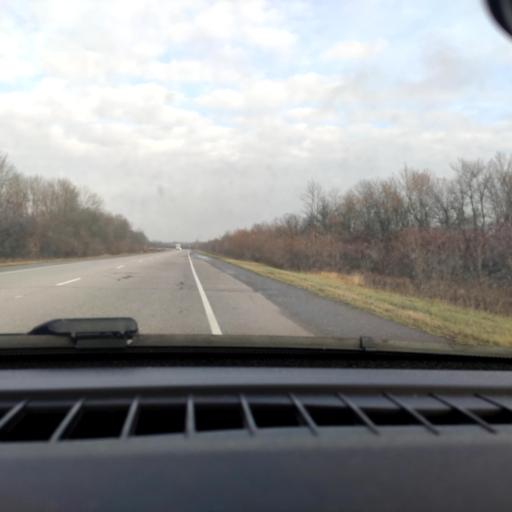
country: RU
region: Voronezj
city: Kolodeznyy
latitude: 51.3008
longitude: 39.0396
